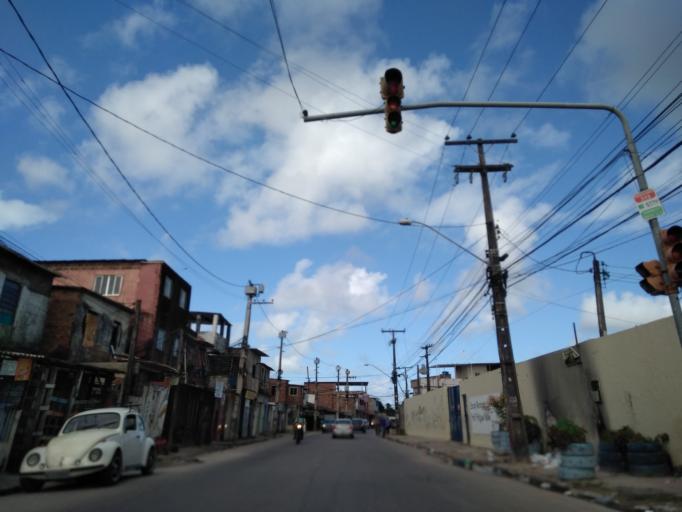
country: BR
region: Pernambuco
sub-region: Recife
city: Recife
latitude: -8.0722
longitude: -34.9259
